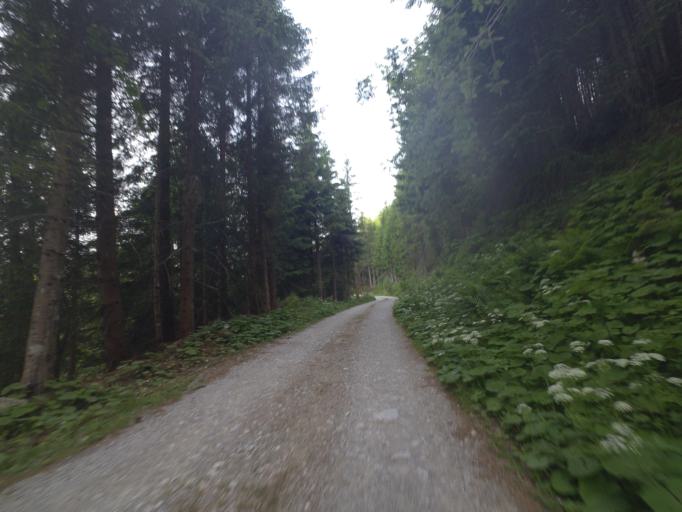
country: AT
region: Salzburg
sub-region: Politischer Bezirk Sankt Johann im Pongau
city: Muhlbach am Hochkonig
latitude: 47.3615
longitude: 13.1110
